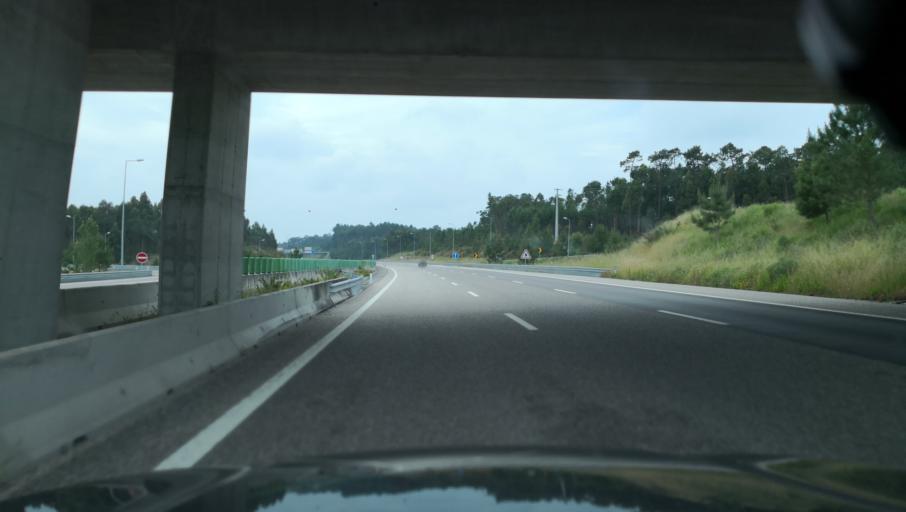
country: PT
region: Coimbra
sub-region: Figueira da Foz
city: Lavos
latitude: 40.0440
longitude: -8.8124
